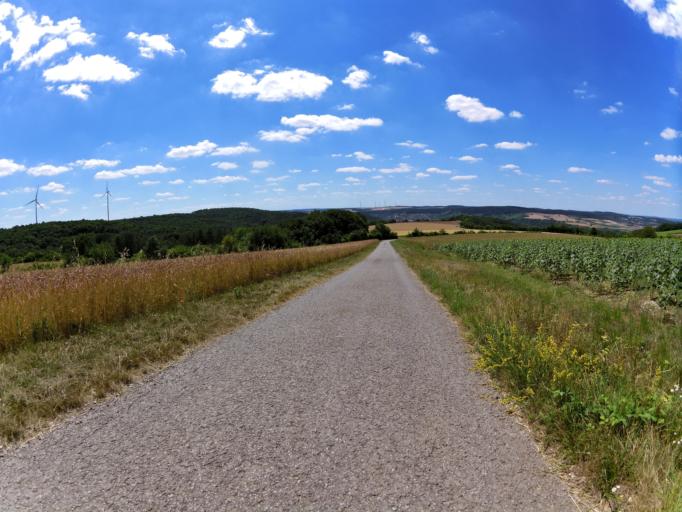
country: DE
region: Bavaria
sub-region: Regierungsbezirk Unterfranken
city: Retzstadt
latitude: 49.8921
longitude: 9.8715
